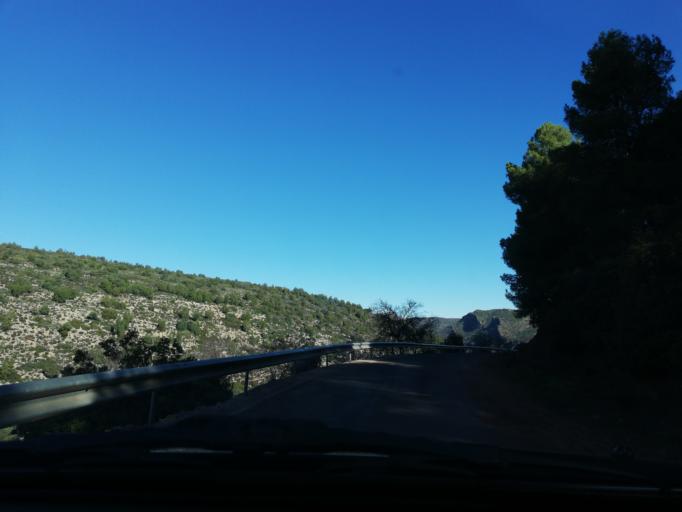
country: MA
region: Souss-Massa-Draa
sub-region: Agadir-Ida-ou-Tnan
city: Tadrart
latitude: 30.6566
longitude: -9.4871
